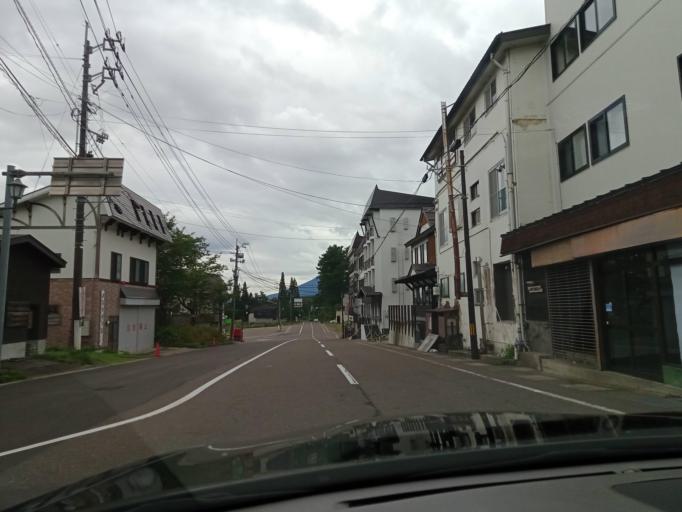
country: JP
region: Niigata
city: Arai
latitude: 36.8921
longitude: 138.1774
